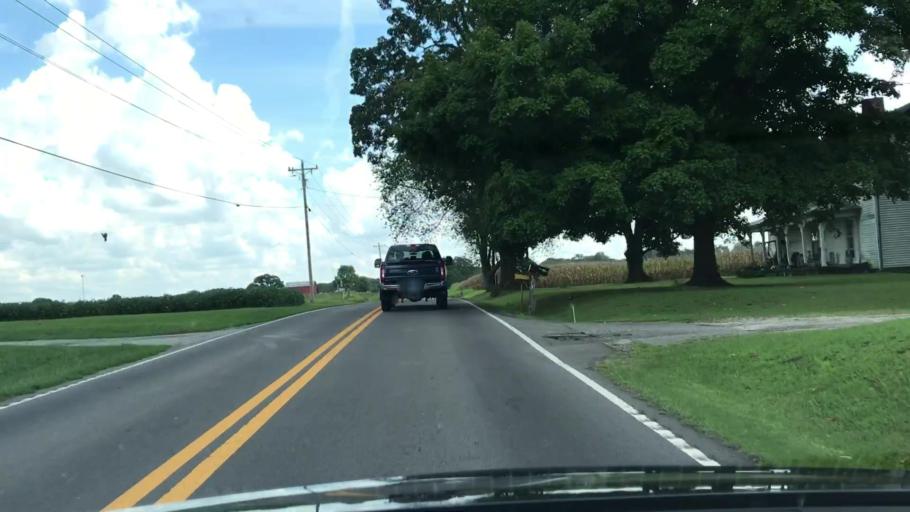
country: US
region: Tennessee
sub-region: Robertson County
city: Springfield
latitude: 36.5550
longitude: -86.8220
